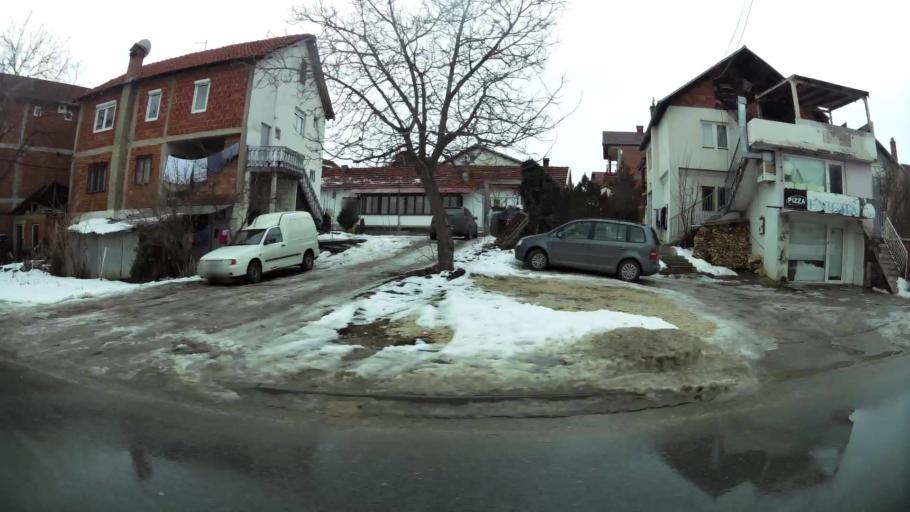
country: XK
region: Pristina
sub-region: Komuna e Prishtines
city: Pristina
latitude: 42.6784
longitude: 21.1727
